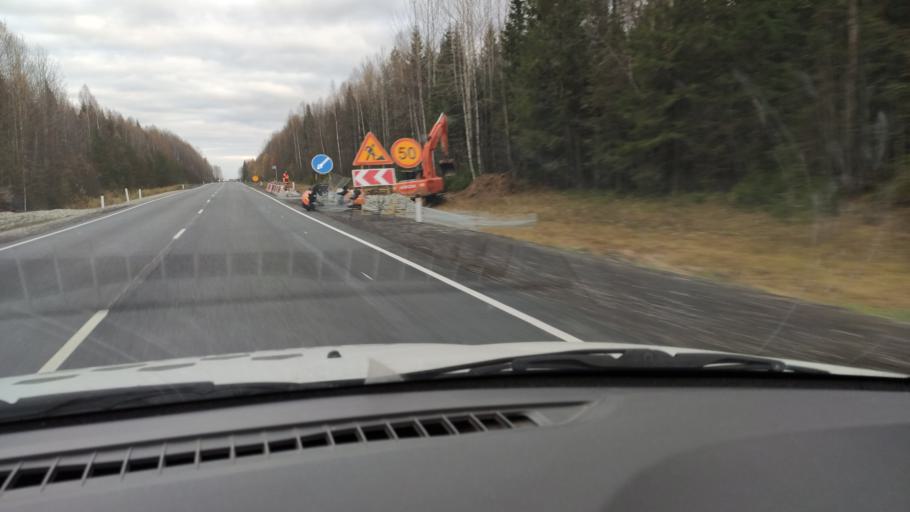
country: RU
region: Kirov
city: Chernaya Kholunitsa
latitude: 58.8793
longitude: 51.4498
